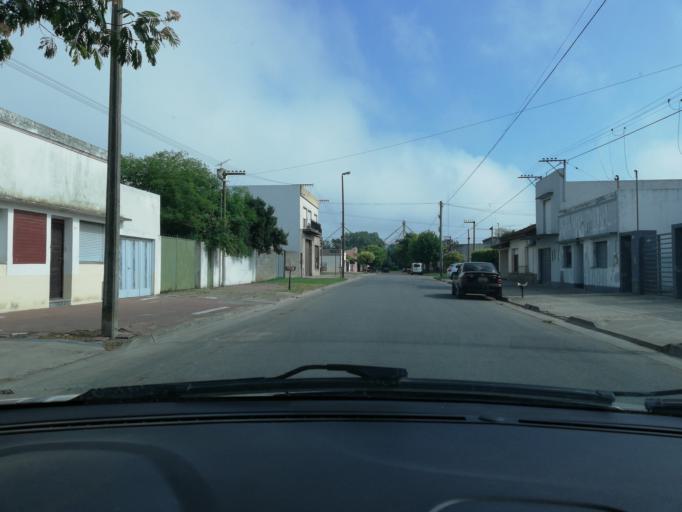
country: AR
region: Buenos Aires
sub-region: Partido de Balcarce
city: Balcarce
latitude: -37.8377
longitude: -58.2645
